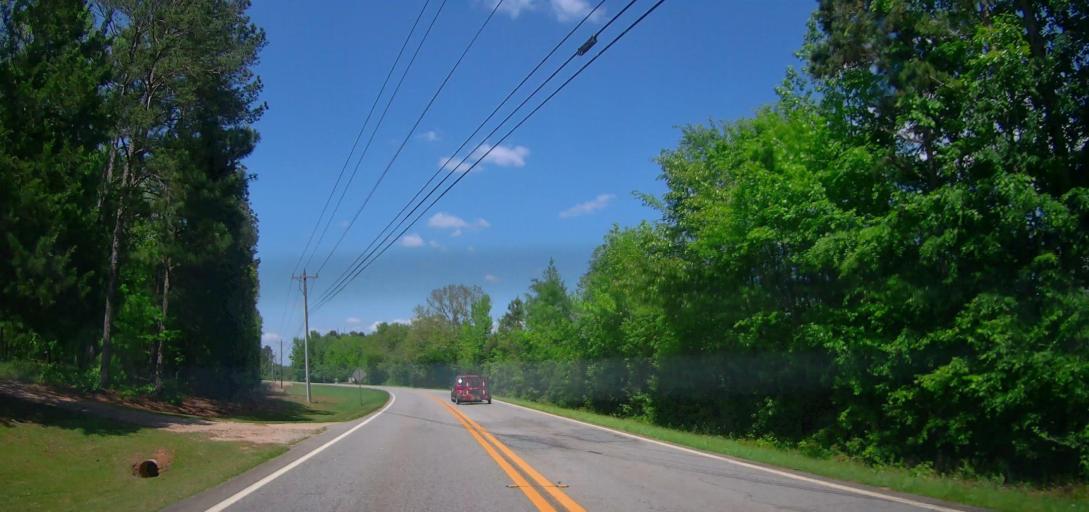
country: US
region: Georgia
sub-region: Putnam County
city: Eatonton
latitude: 33.3052
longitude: -83.3021
